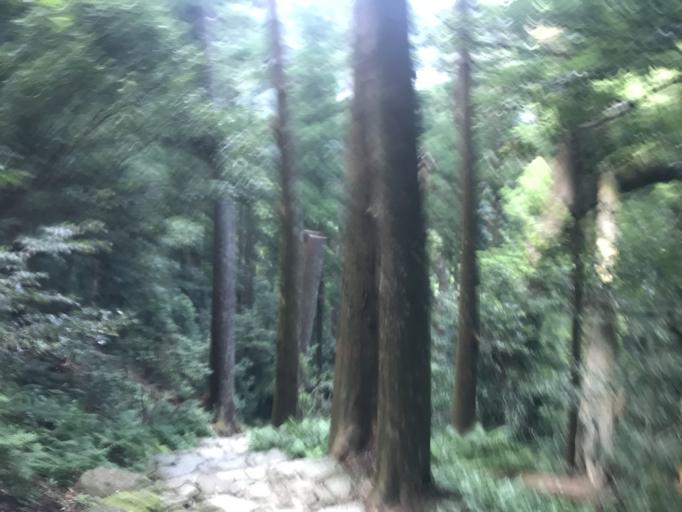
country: JP
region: Wakayama
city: Shingu
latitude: 33.6718
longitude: 135.8897
